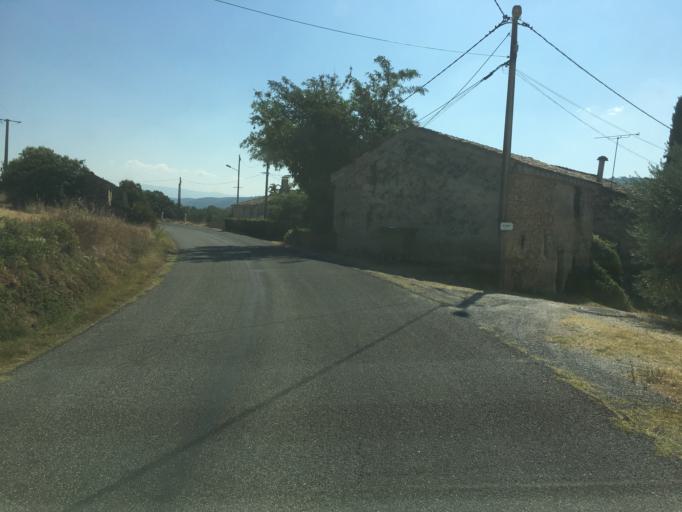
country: FR
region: Provence-Alpes-Cote d'Azur
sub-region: Departement des Alpes-de-Haute-Provence
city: Oraison
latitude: 43.8872
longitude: 5.9438
